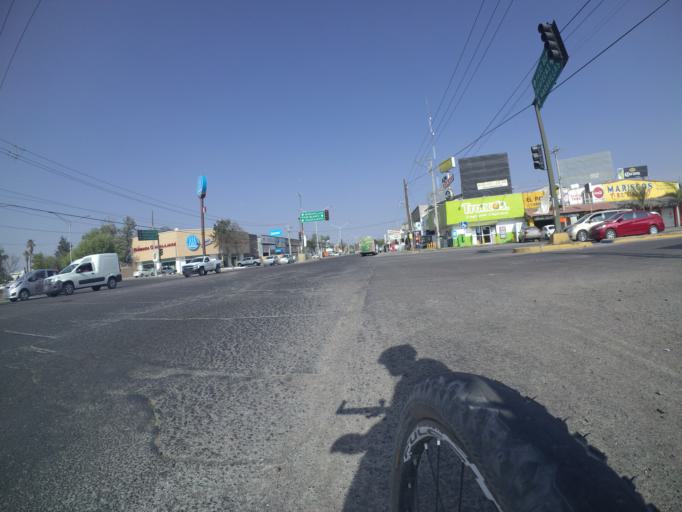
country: MX
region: Aguascalientes
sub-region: Jesus Maria
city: Tepetates
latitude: 21.9507
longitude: -102.3239
